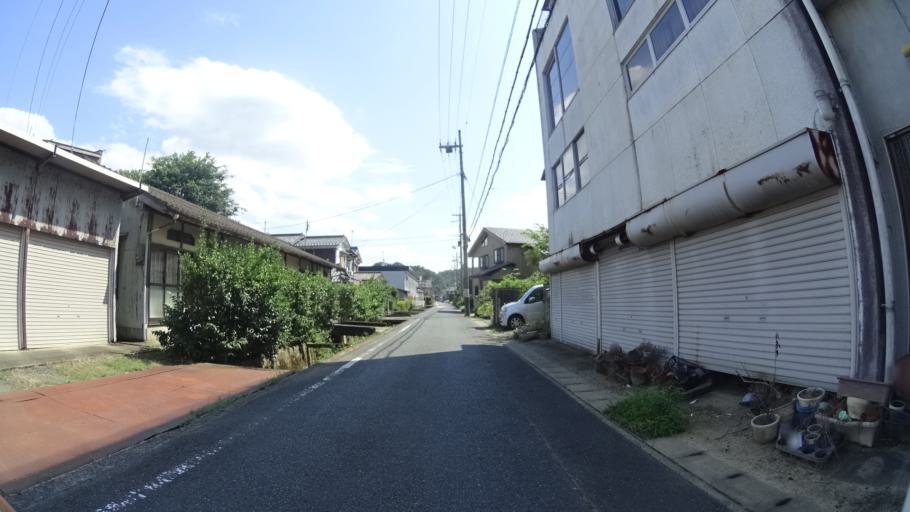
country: JP
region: Kyoto
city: Maizuru
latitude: 35.4405
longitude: 135.3245
